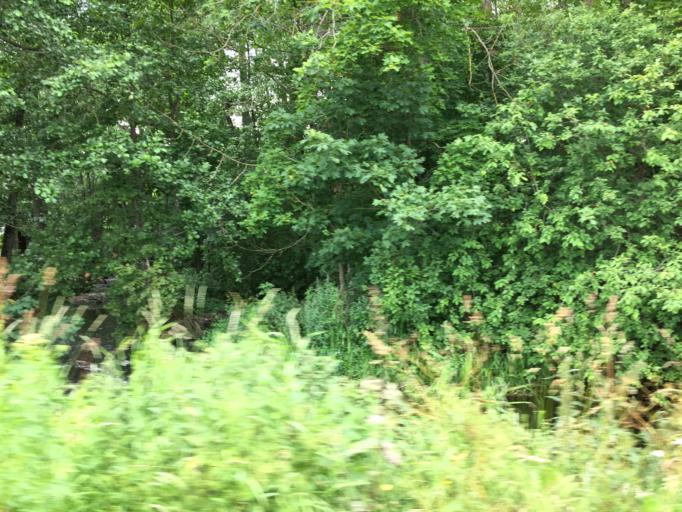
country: SE
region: Vaestmanland
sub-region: Norbergs Kommun
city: Norberg
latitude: 60.0300
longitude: 15.9638
